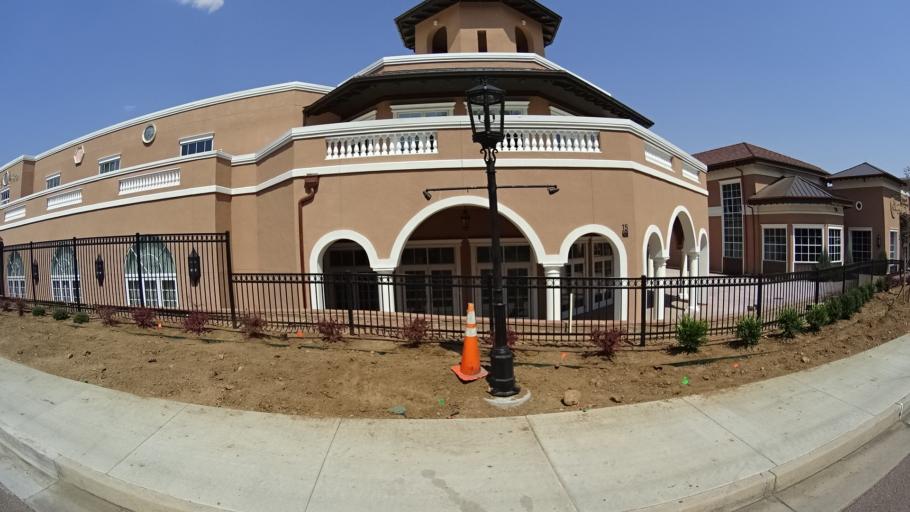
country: US
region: Colorado
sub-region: El Paso County
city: Colorado Springs
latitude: 38.7928
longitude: -104.8511
